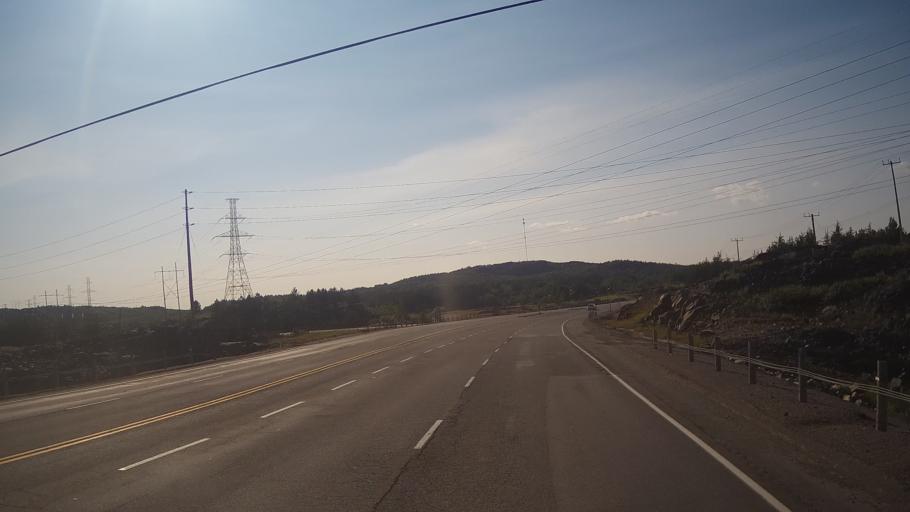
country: CA
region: Ontario
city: Greater Sudbury
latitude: 46.5044
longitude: -81.0446
